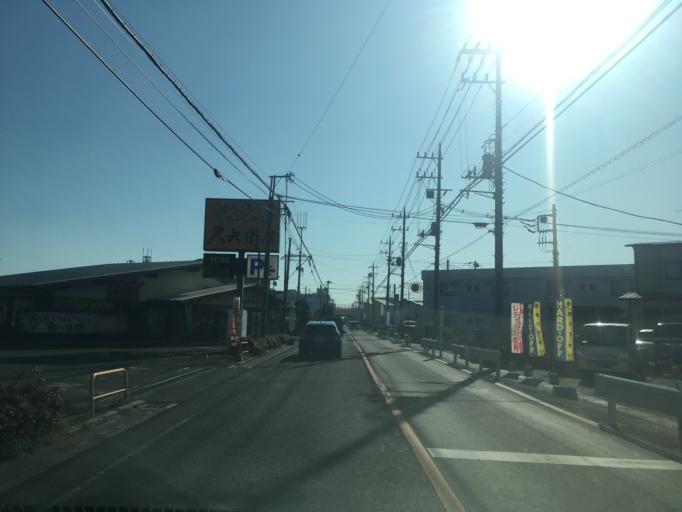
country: JP
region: Saitama
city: Kawagoe
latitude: 35.8840
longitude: 139.4763
